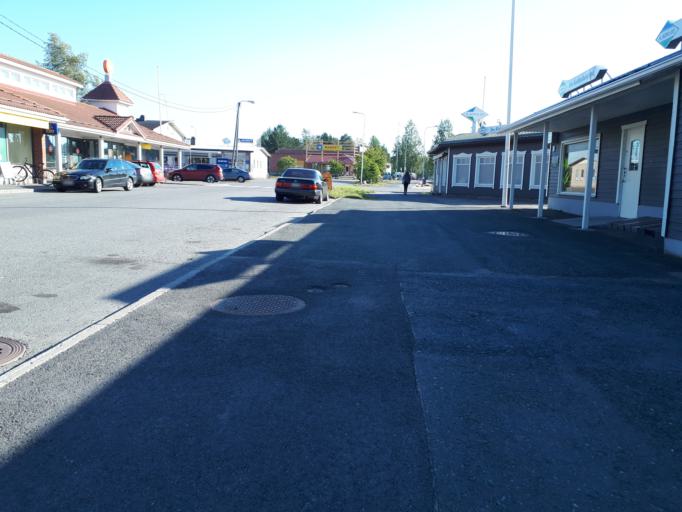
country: FI
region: Northern Ostrobothnia
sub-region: Oulunkaari
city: Ii
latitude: 65.3235
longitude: 25.3777
